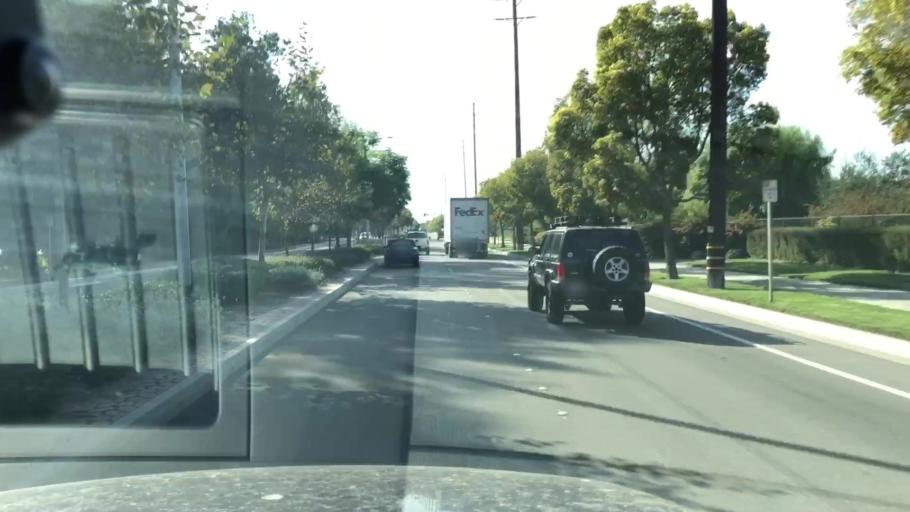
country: US
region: California
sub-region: Ventura County
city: Camarillo
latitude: 34.2055
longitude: -119.0225
